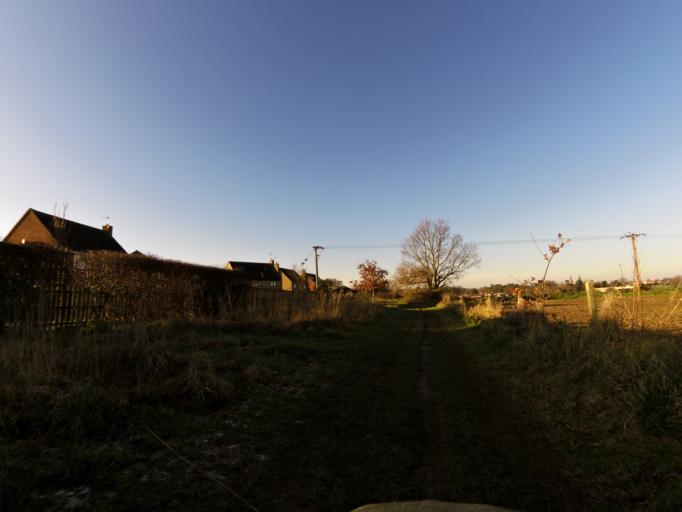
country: GB
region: England
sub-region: Norfolk
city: Aylsham
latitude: 52.7891
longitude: 1.2634
